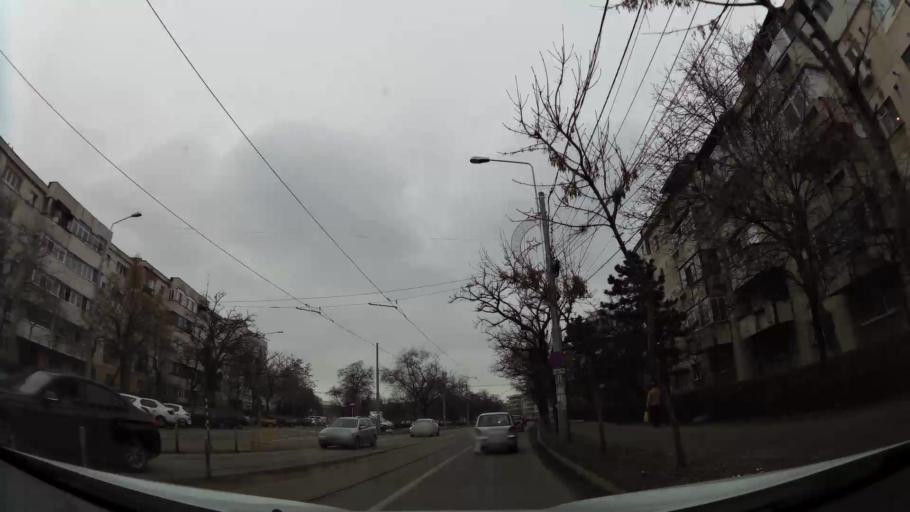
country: RO
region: Prahova
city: Ploiesti
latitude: 44.9322
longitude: 26.0315
